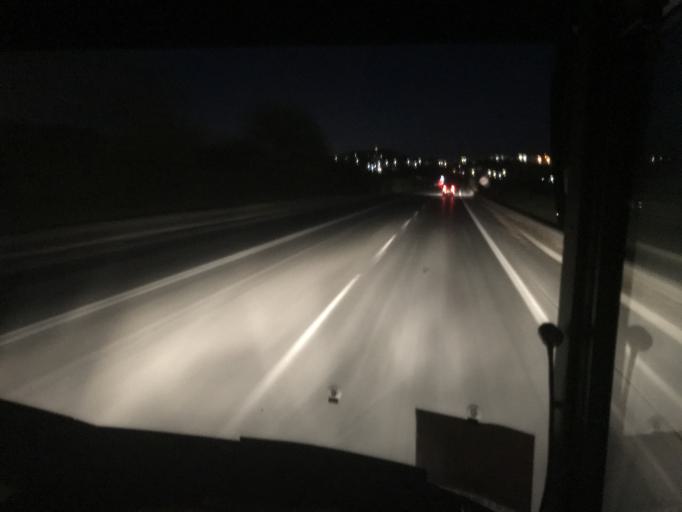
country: GR
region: Crete
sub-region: Nomos Irakleiou
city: Skalanion
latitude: 35.2688
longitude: 25.1848
